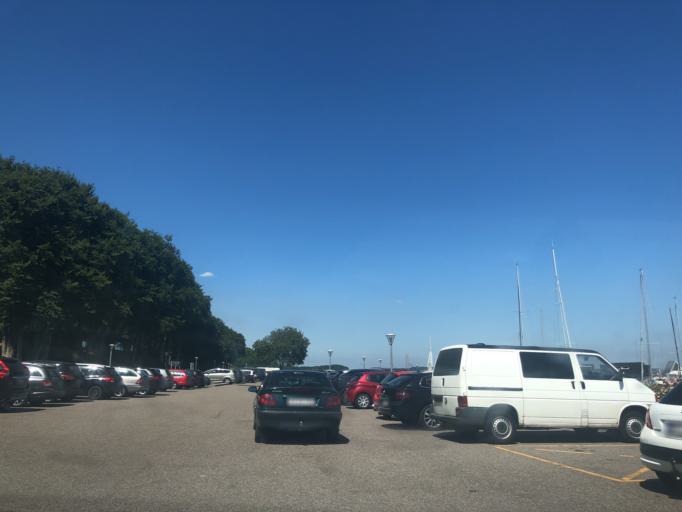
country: DK
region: Central Jutland
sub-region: Skive Kommune
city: Skive
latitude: 56.5749
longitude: 9.0514
